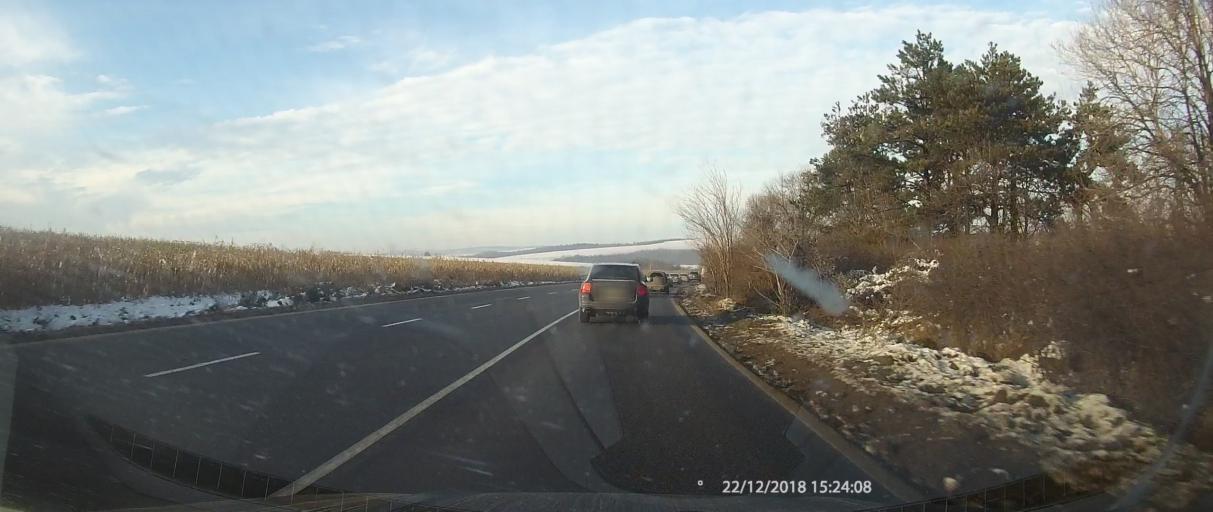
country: BG
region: Ruse
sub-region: Obshtina Ivanovo
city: Ivanovo
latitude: 43.7328
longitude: 25.9142
